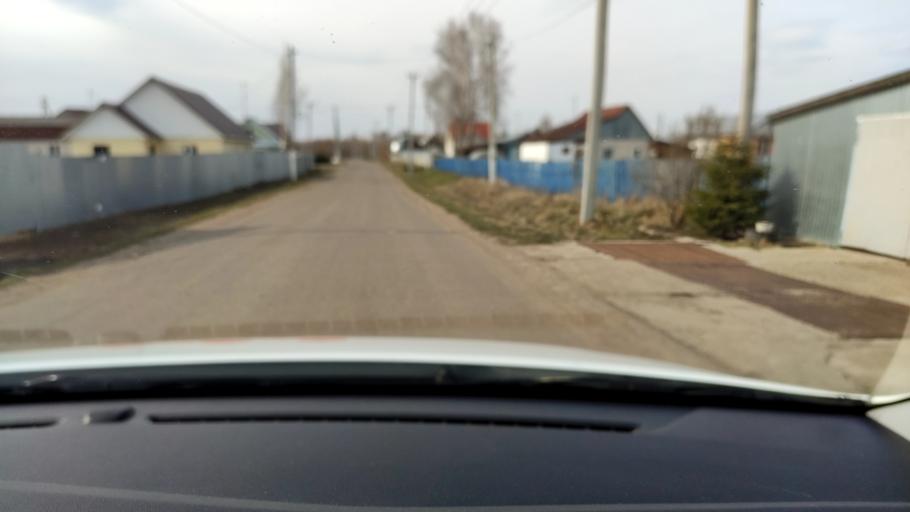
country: RU
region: Tatarstan
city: Stolbishchi
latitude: 55.6448
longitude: 49.3123
